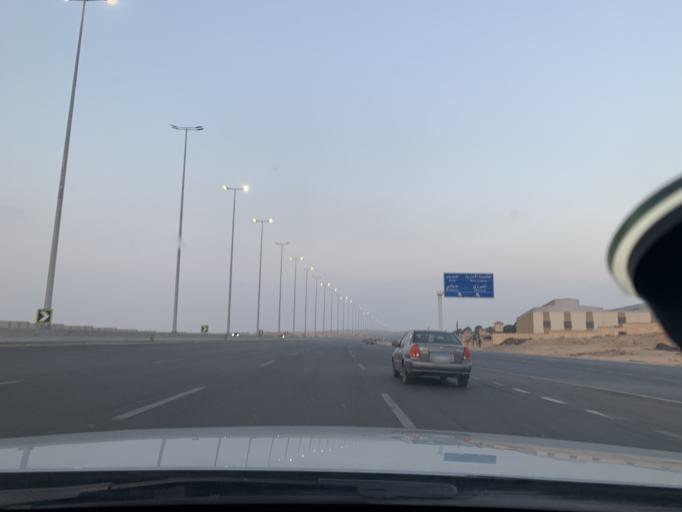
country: EG
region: Muhafazat al Qalyubiyah
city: Al Khankah
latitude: 30.0892
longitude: 31.4629
